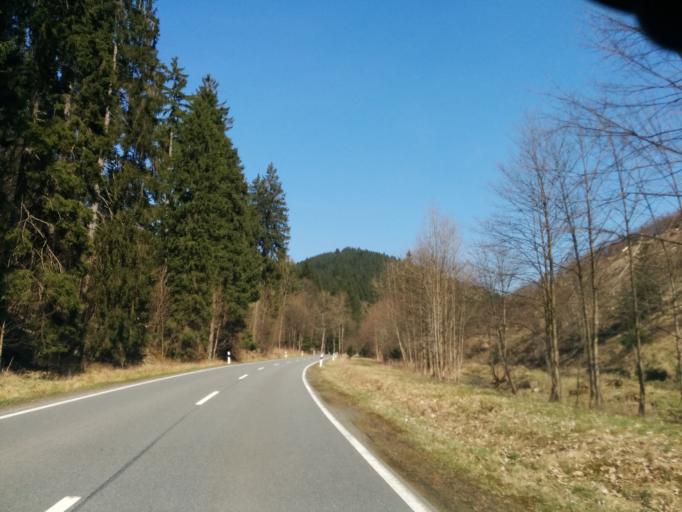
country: DE
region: Lower Saxony
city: Sankt Andreasberg
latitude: 51.6844
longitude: 10.4973
